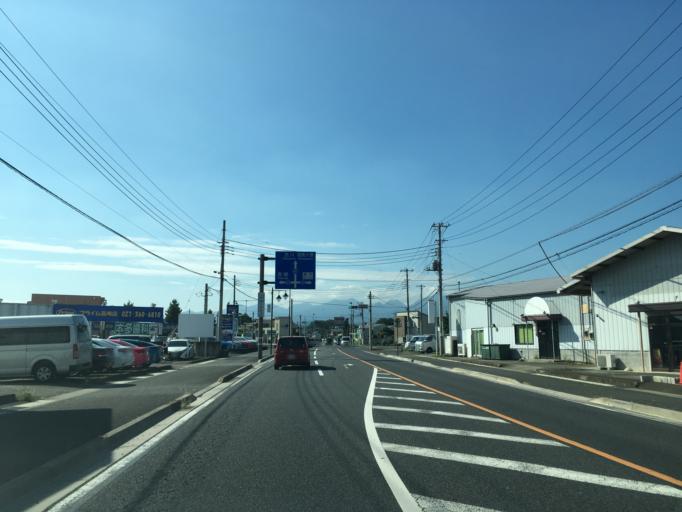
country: JP
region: Gunma
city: Kanekomachi
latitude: 36.3893
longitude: 139.0219
